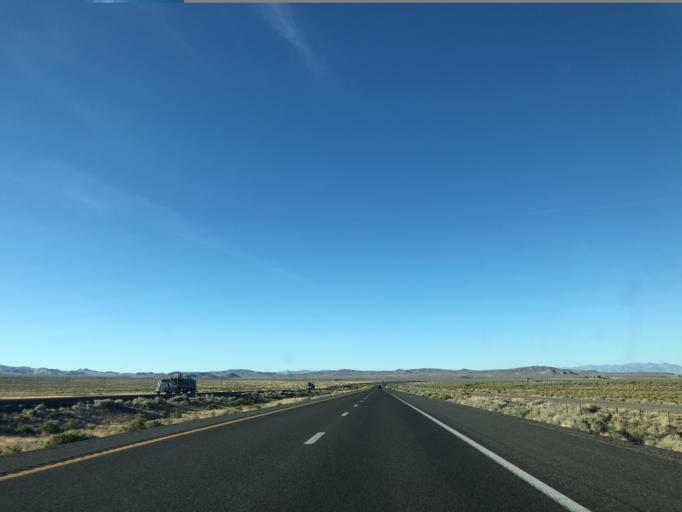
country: US
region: Nevada
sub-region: Pershing County
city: Lovelock
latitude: 40.0456
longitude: -118.6614
